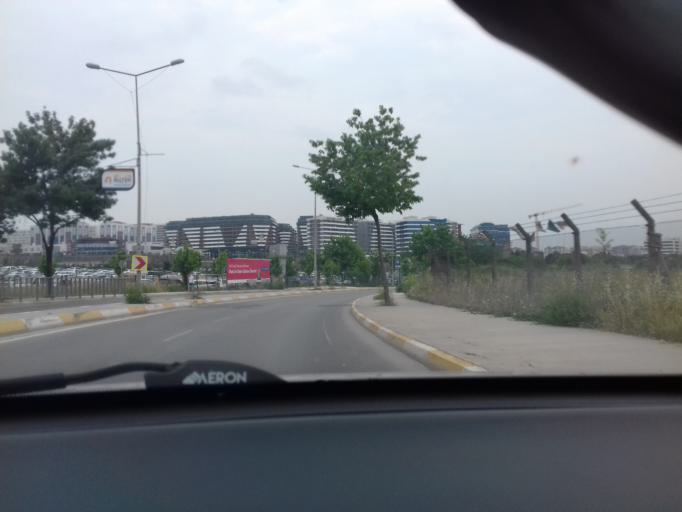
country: TR
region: Istanbul
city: Sultanbeyli
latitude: 40.9226
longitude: 29.3090
